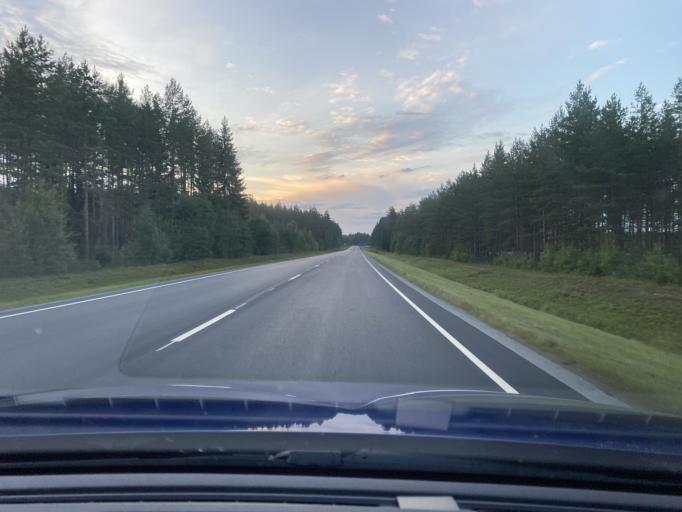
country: FI
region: Satakunta
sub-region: Pohjois-Satakunta
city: Honkajoki
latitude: 62.0088
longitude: 22.2284
